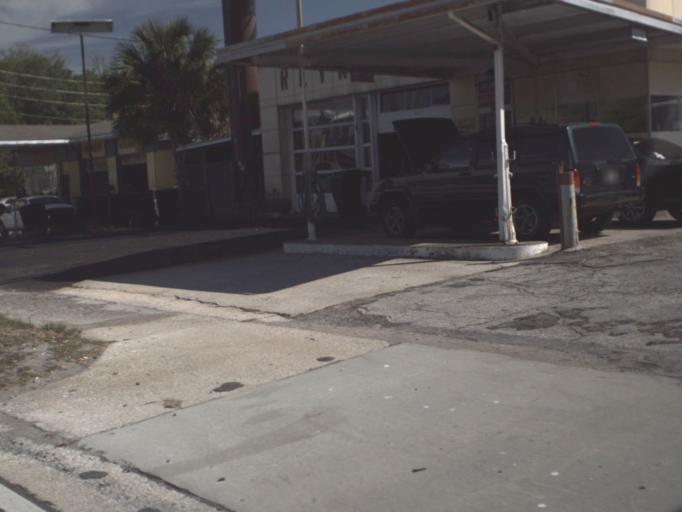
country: US
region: Florida
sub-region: Lake County
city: Leesburg
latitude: 28.8309
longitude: -81.8874
